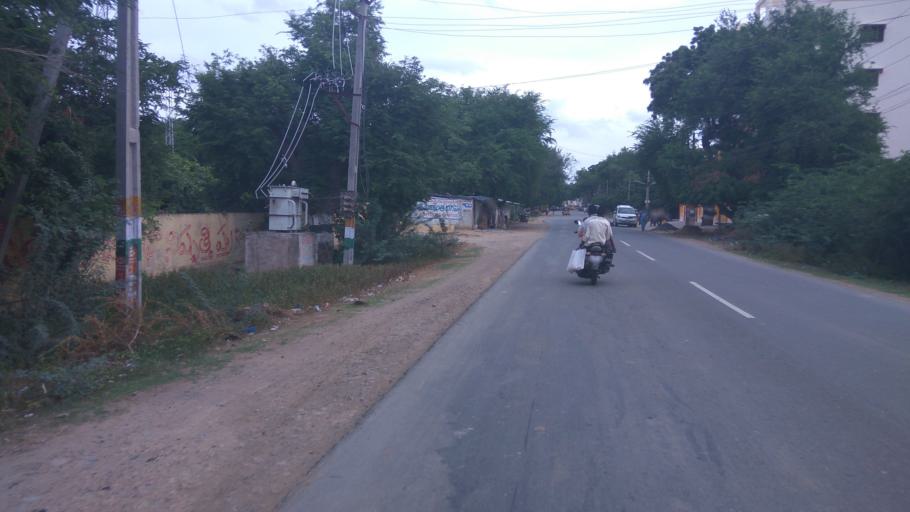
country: IN
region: Andhra Pradesh
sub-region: Prakasam
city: Cumbum
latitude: 15.5906
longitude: 79.1157
